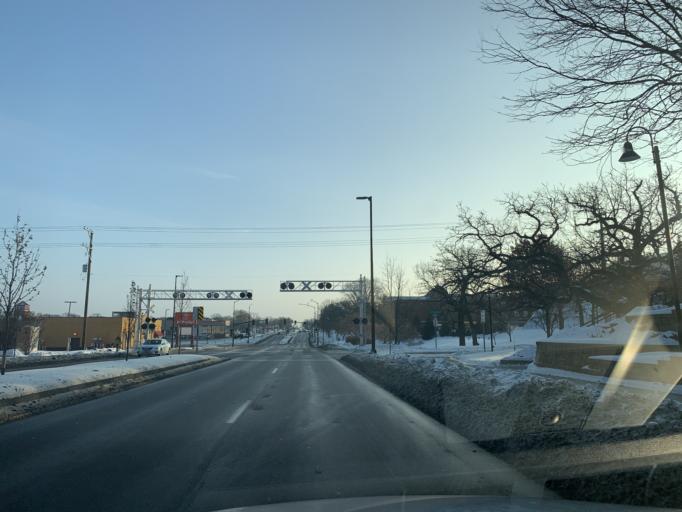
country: US
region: Minnesota
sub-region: Hennepin County
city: Richfield
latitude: 44.8834
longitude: -93.2840
